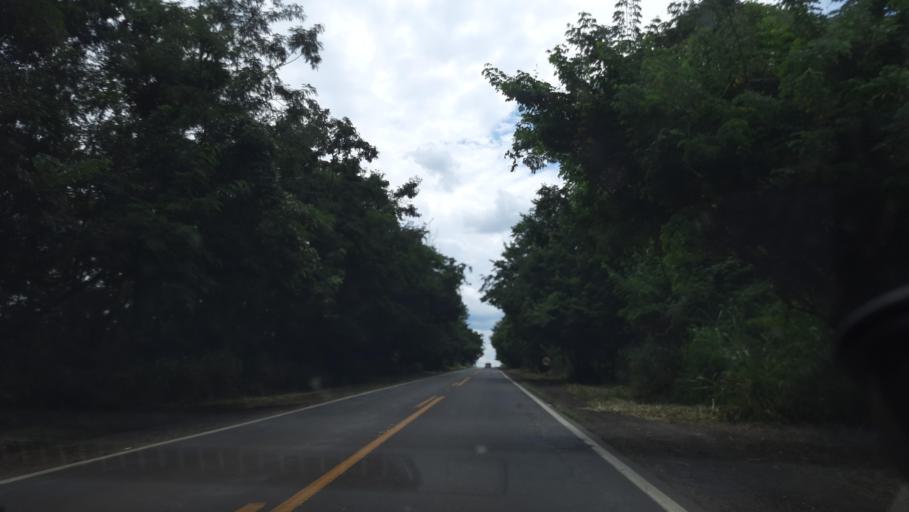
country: BR
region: Sao Paulo
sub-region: Mococa
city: Mococa
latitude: -21.4987
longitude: -47.0634
